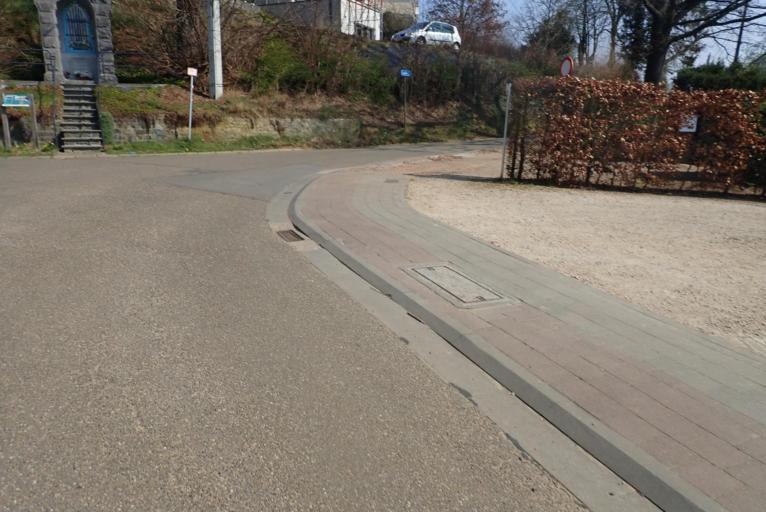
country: BE
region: Flanders
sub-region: Provincie Vlaams-Brabant
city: Aarschot
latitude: 50.9884
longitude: 4.8515
